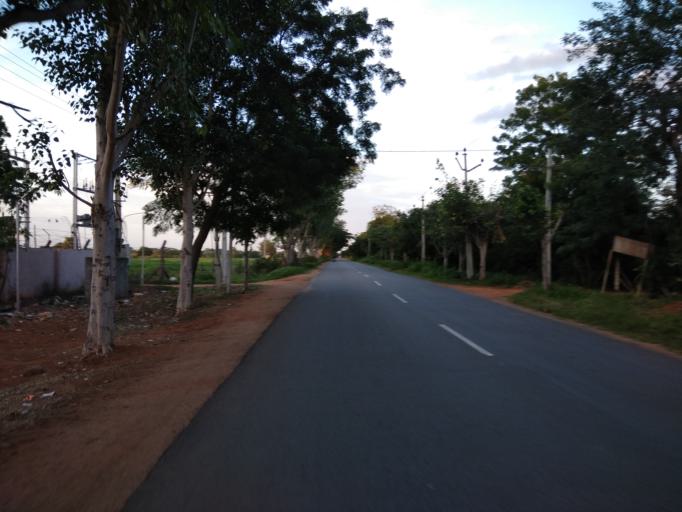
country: IN
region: Telangana
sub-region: Rangareddi
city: Sriramnagar
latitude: 17.2545
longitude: 78.3089
